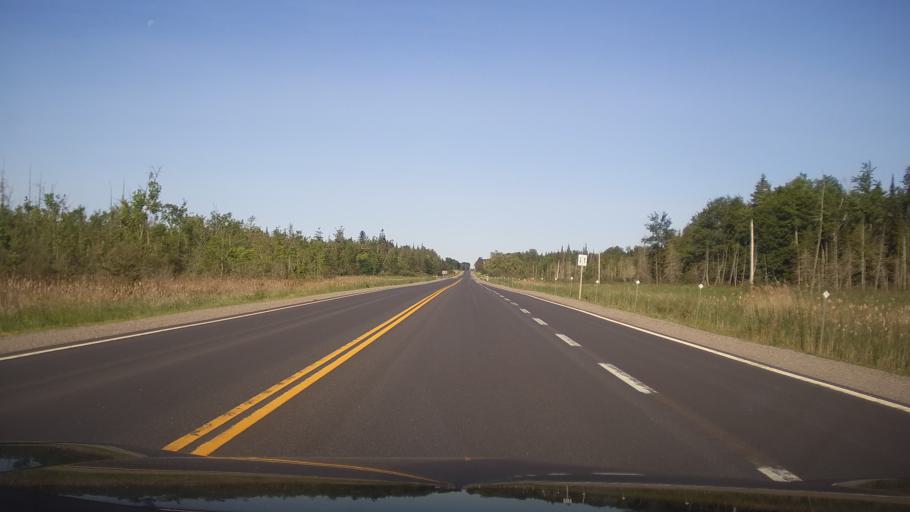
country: CA
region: Ontario
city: Belleville
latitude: 44.5279
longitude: -77.4067
